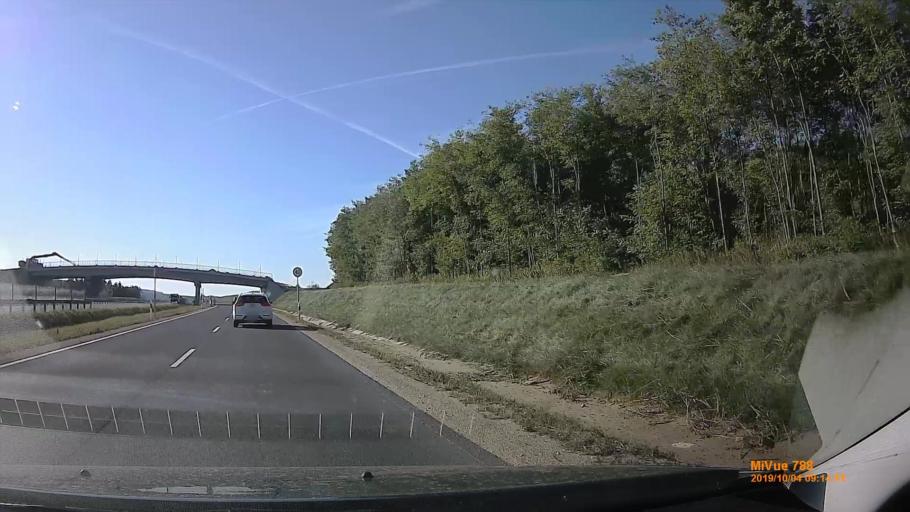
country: HU
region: Somogy
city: Karad
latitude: 46.6392
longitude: 17.7879
